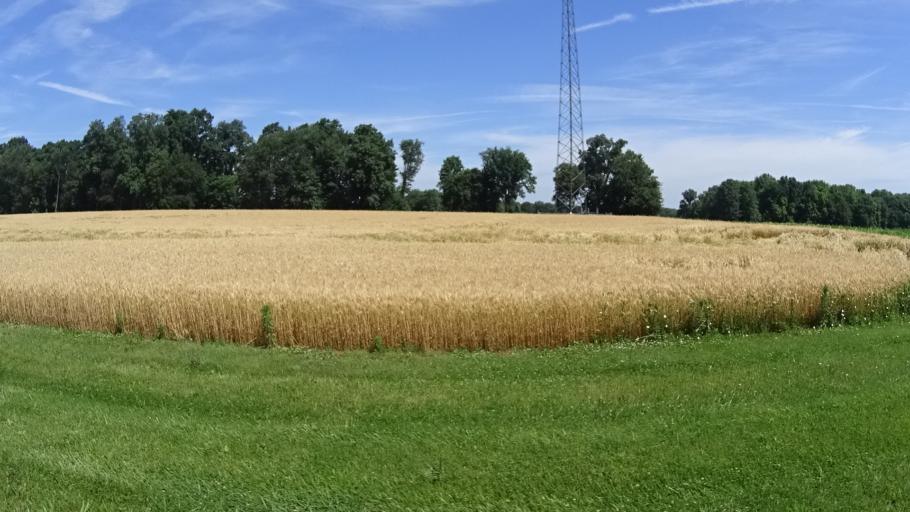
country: US
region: Ohio
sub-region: Huron County
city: Wakeman
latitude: 41.3446
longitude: -82.4558
